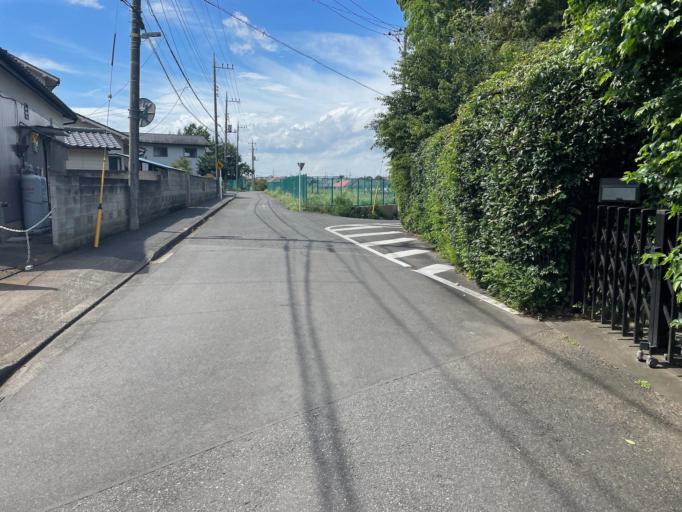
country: JP
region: Tokyo
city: Tanashicho
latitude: 35.7512
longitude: 139.5248
